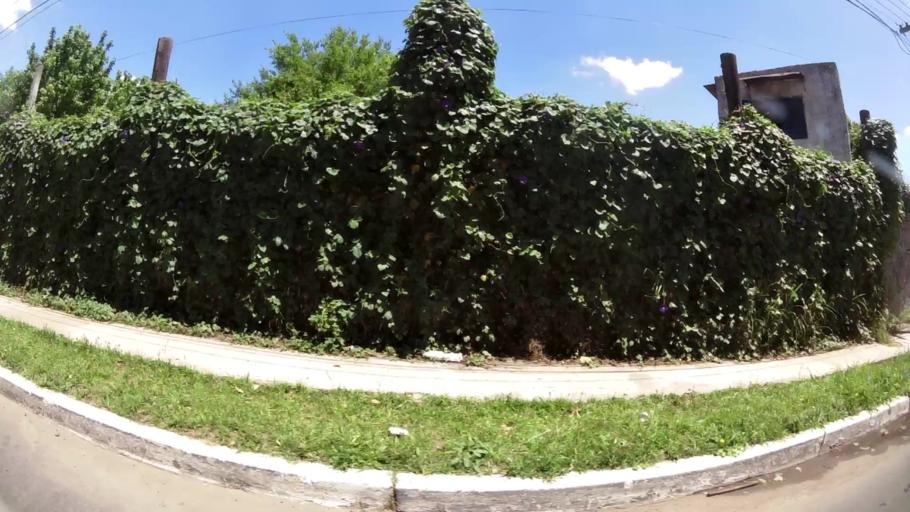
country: AR
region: Buenos Aires
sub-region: Partido de Merlo
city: Merlo
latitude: -34.6576
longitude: -58.7102
